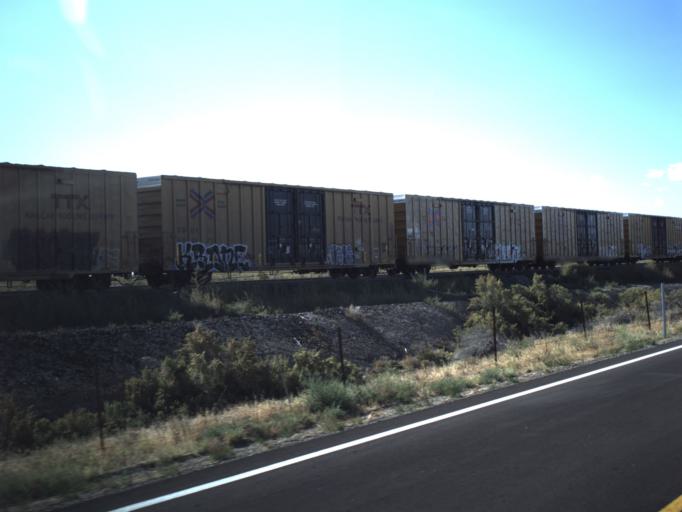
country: US
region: Utah
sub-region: Millard County
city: Delta
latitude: 39.2365
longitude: -112.6654
